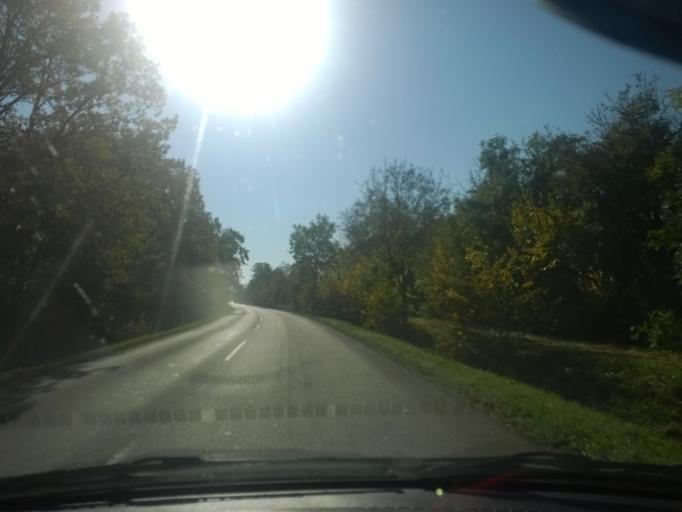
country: HU
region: Csongrad
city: Hodmezovasarhely
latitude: 46.4907
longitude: 20.3136
